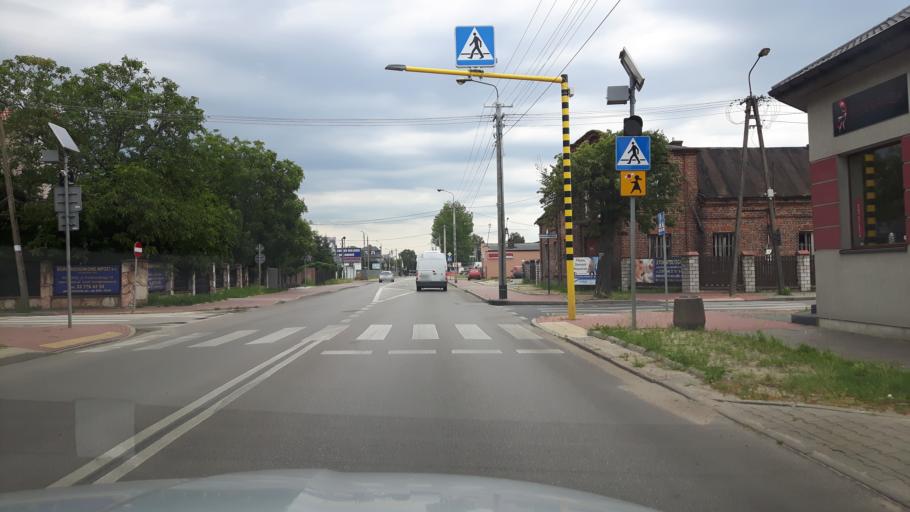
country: PL
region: Masovian Voivodeship
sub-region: Powiat wolominski
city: Wolomin
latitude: 52.3391
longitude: 21.2441
